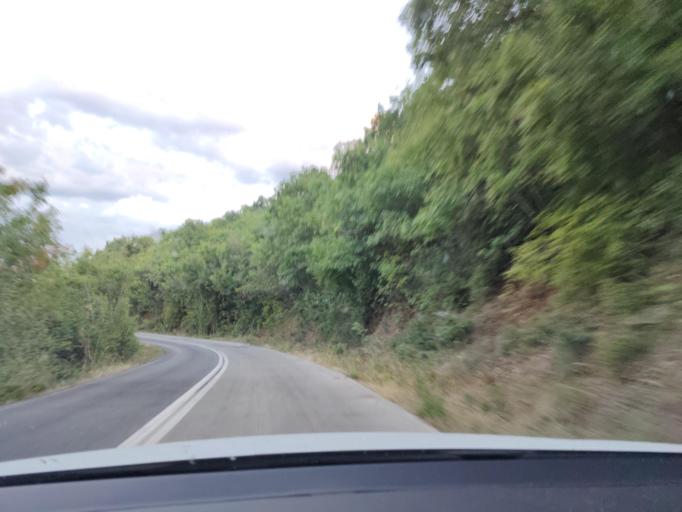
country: GR
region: Central Macedonia
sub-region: Nomos Serron
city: Chrysochorafa
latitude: 41.1714
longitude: 23.1750
